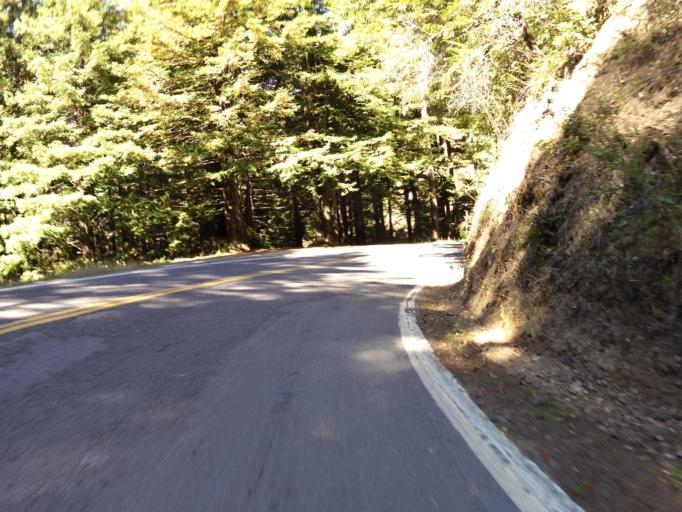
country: US
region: California
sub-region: Humboldt County
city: Redway
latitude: 39.7966
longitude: -123.8176
